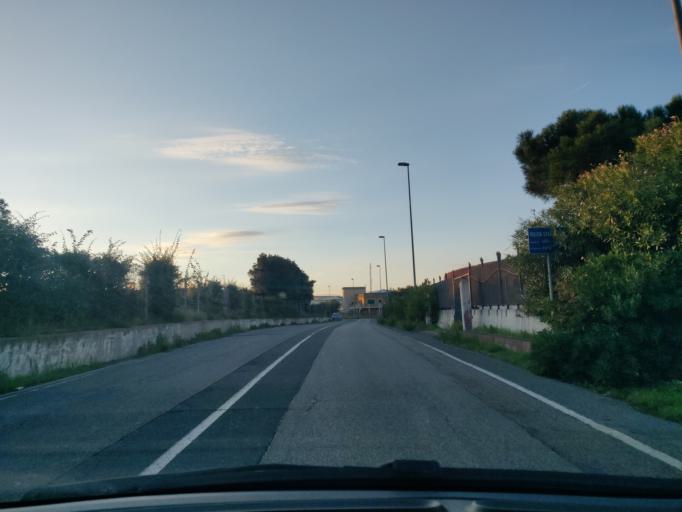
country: IT
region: Latium
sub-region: Citta metropolitana di Roma Capitale
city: Civitavecchia
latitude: 42.1102
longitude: 11.7774
